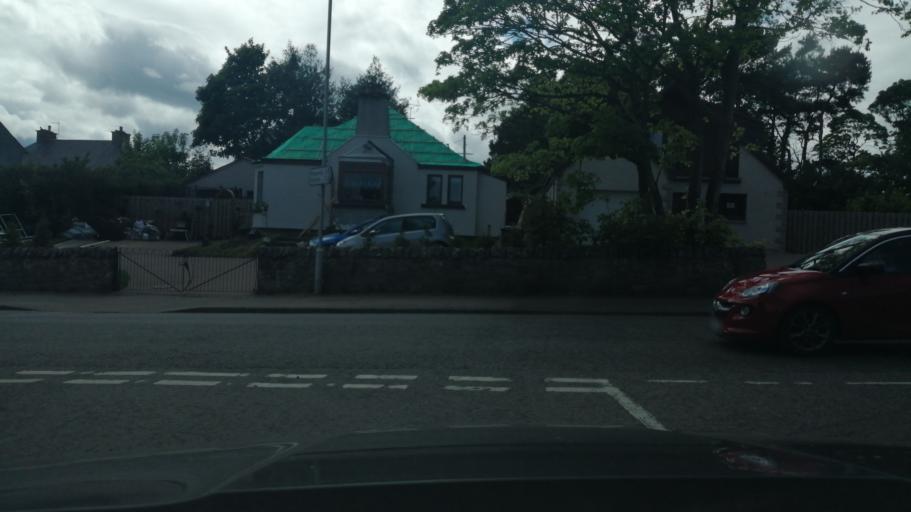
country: GB
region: Scotland
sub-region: Moray
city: Elgin
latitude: 57.6546
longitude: -3.3010
